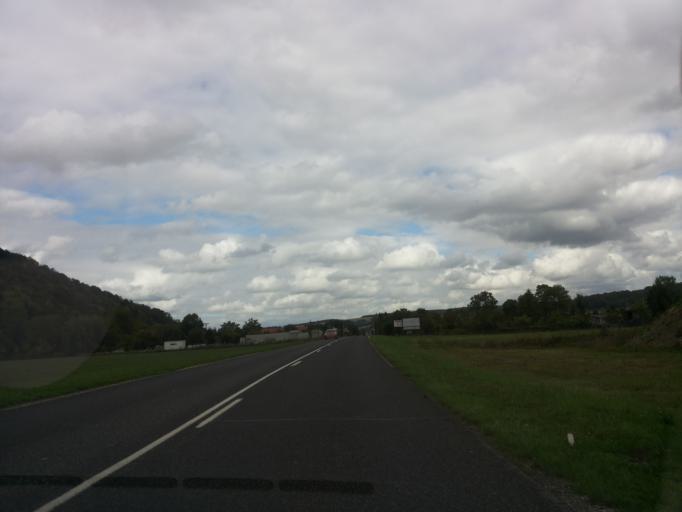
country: FR
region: Lorraine
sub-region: Departement de la Meuse
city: Ligny-en-Barrois
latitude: 48.6710
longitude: 5.3263
